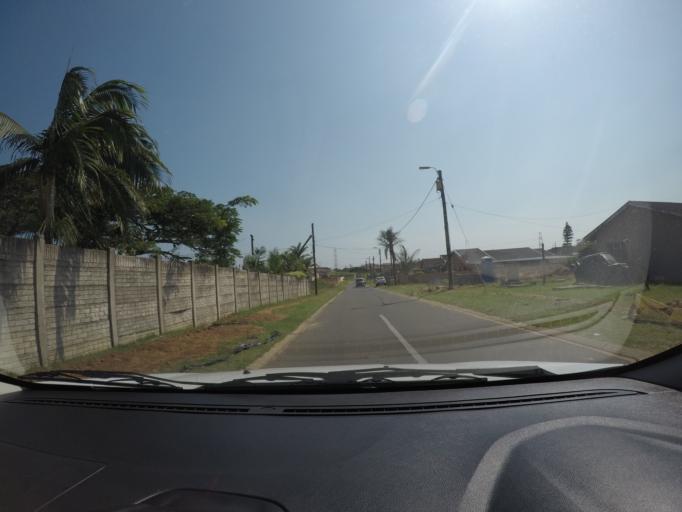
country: ZA
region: KwaZulu-Natal
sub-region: uThungulu District Municipality
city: Richards Bay
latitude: -28.7239
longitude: 32.0388
